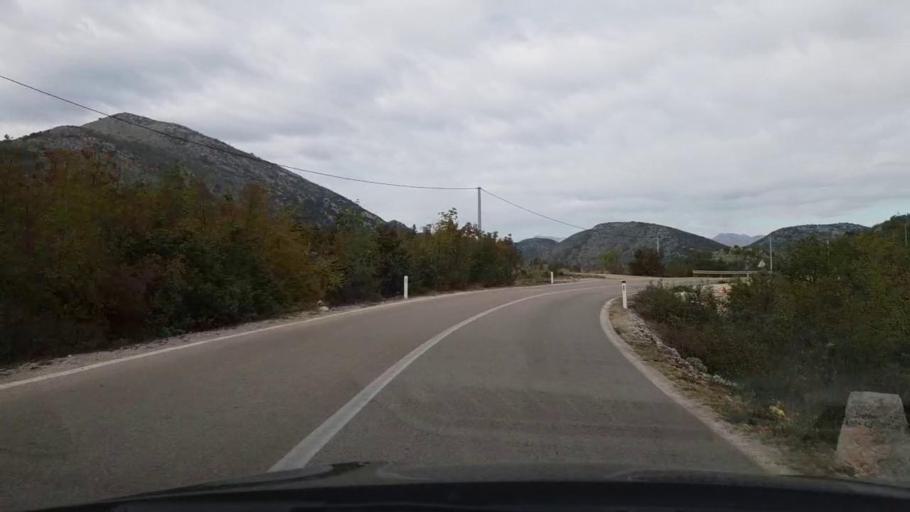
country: HR
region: Dubrovacko-Neretvanska
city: Cibaca
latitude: 42.6572
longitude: 18.2110
